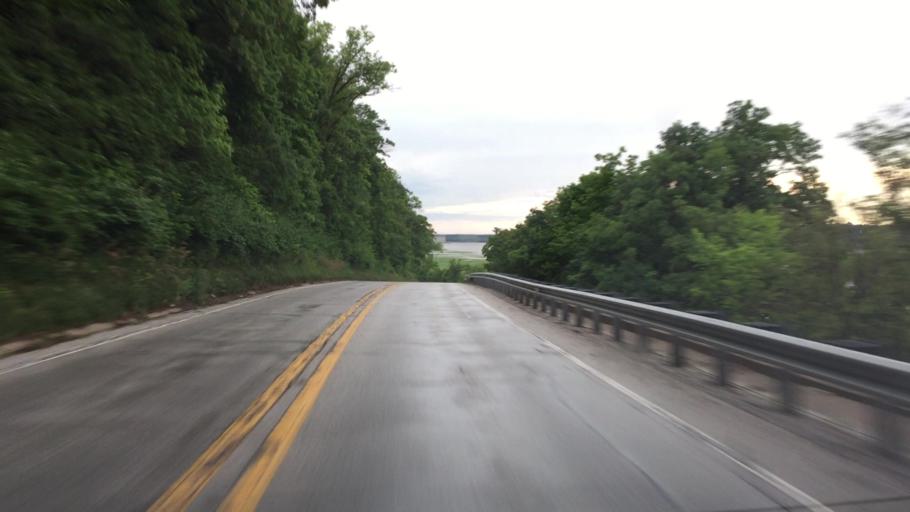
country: US
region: Iowa
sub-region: Lee County
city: Keokuk
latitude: 40.4408
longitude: -91.3716
